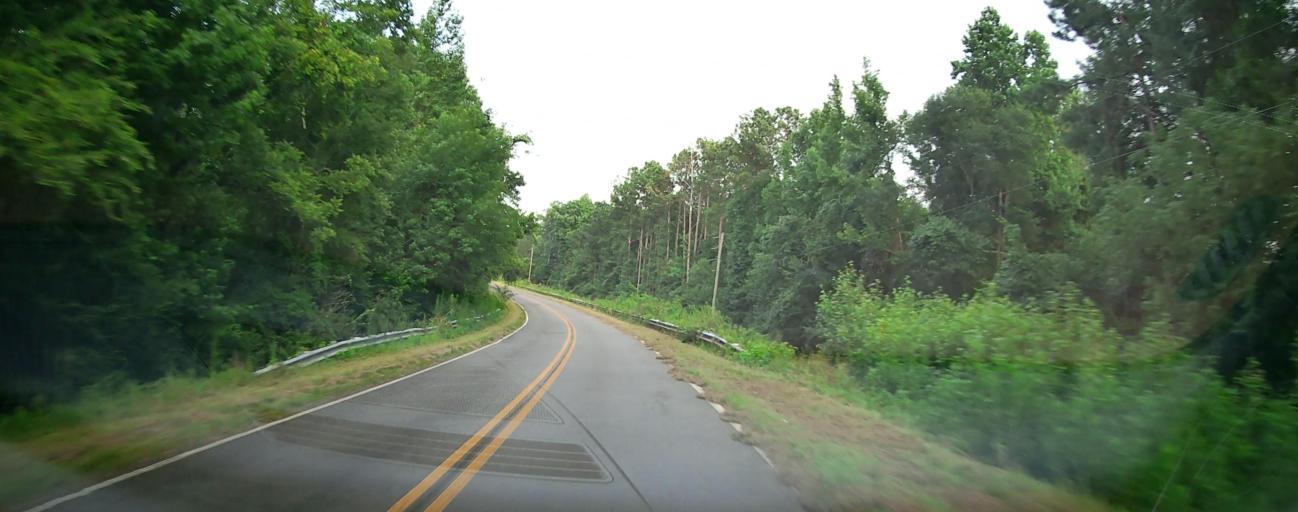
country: US
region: Georgia
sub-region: Crawford County
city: Roberta
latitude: 32.6722
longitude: -84.0801
